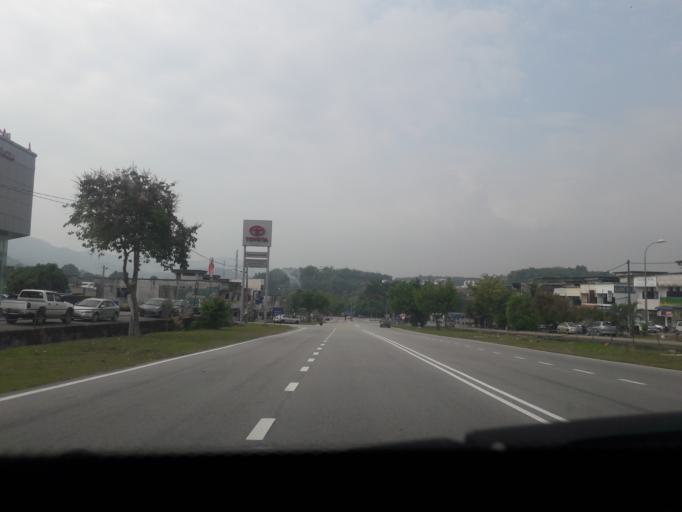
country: MY
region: Kedah
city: Kulim
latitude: 5.3548
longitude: 100.5308
